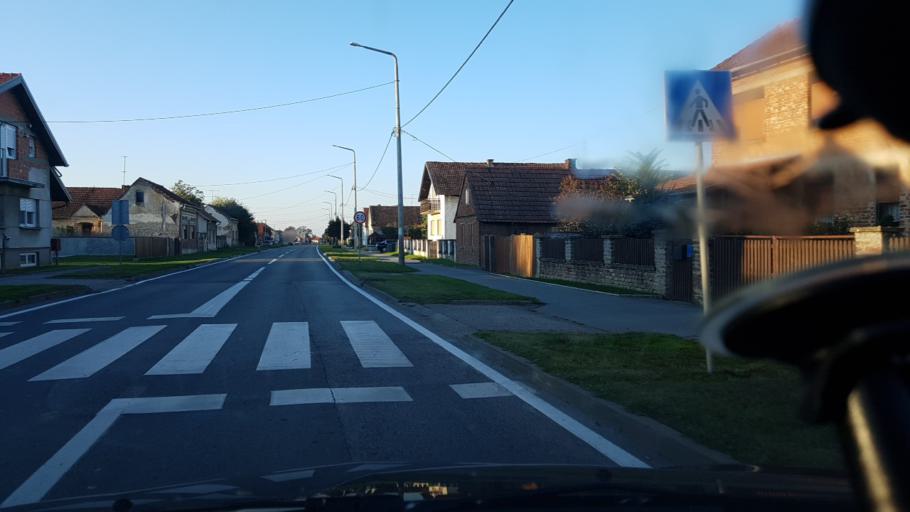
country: HR
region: Koprivnicko-Krizevacka
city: Virje
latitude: 46.0807
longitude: 16.9520
